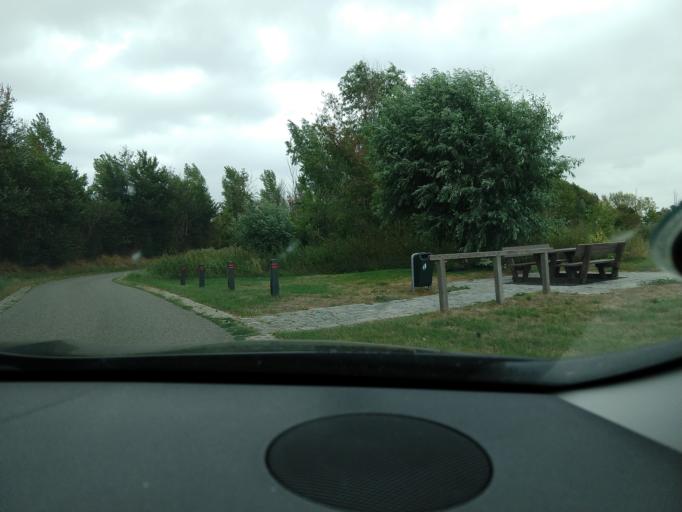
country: NL
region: Zeeland
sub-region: Gemeente Hulst
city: Hulst
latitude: 51.3482
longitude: 4.0497
